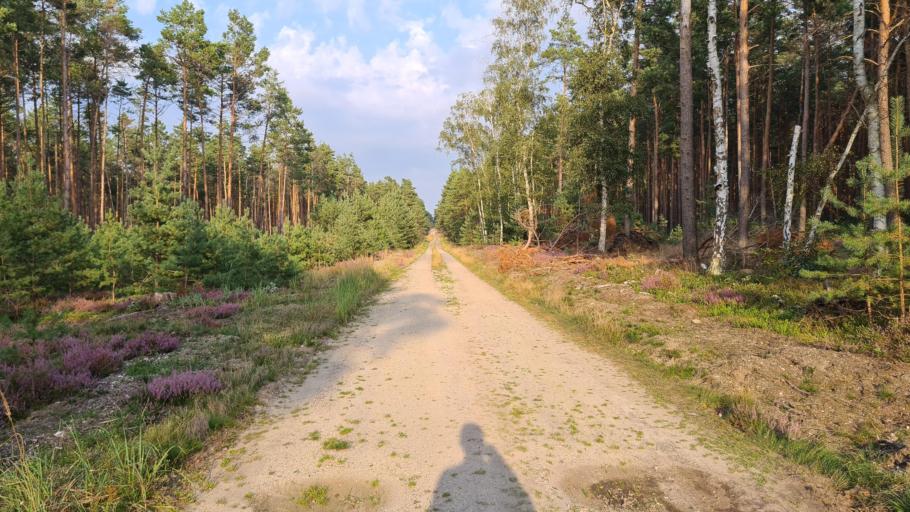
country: DE
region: Brandenburg
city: Trobitz
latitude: 51.6356
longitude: 13.4601
